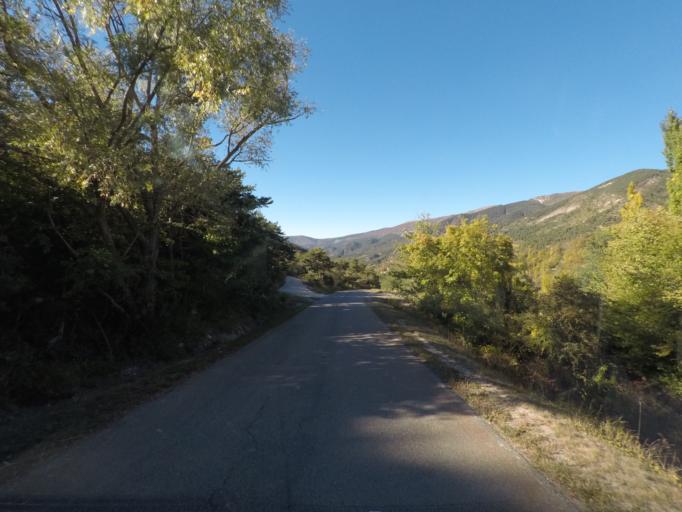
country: FR
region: Provence-Alpes-Cote d'Azur
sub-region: Departement des Hautes-Alpes
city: Serres
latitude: 44.4388
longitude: 5.5584
